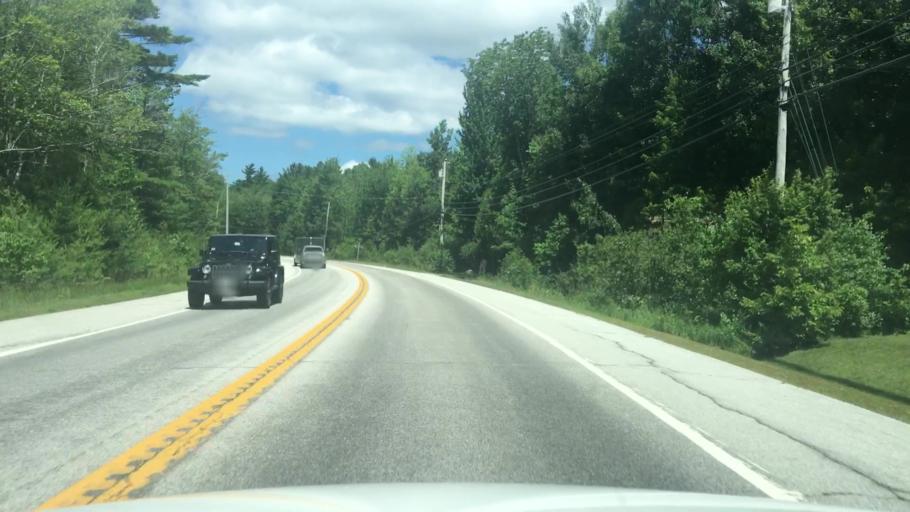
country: US
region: Maine
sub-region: Waldo County
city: Northport
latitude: 44.3547
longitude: -68.9676
